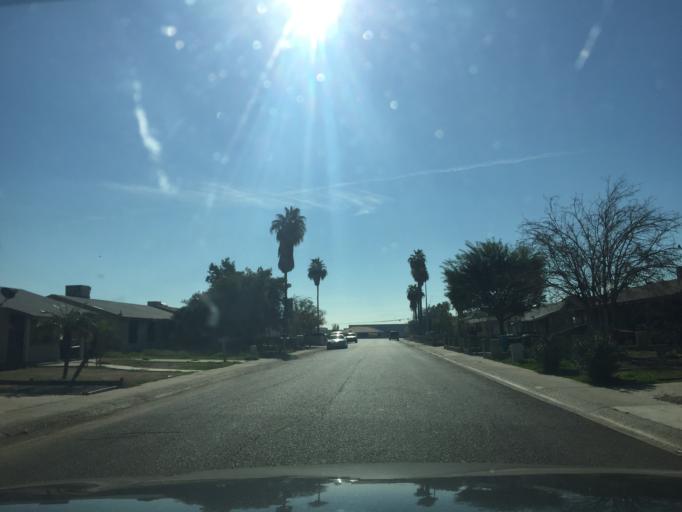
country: US
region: Arizona
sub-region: Maricopa County
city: Tolleson
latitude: 33.4672
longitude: -112.2172
